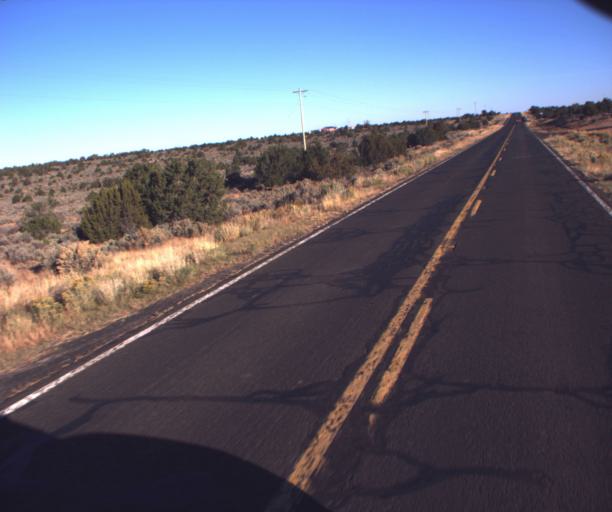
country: US
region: Arizona
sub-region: Apache County
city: Ganado
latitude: 35.5727
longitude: -109.5350
